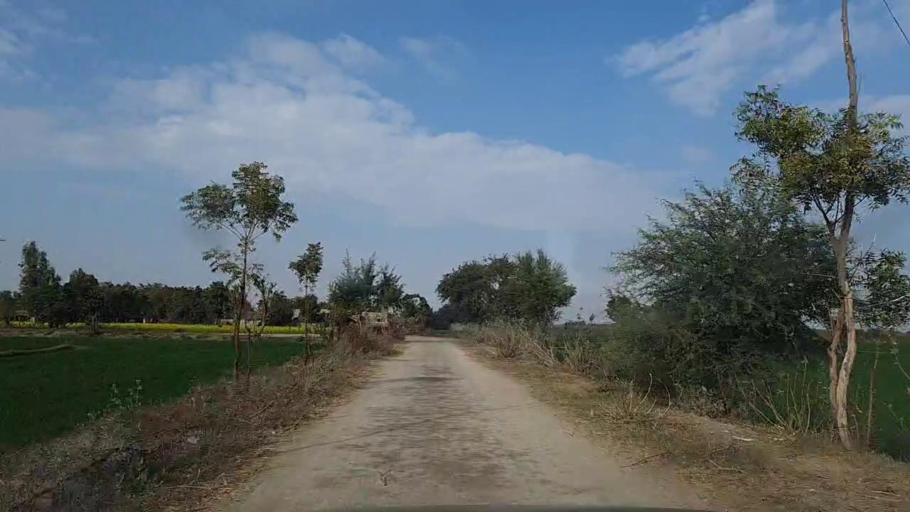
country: PK
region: Sindh
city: Sanghar
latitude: 26.2433
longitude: 69.0191
